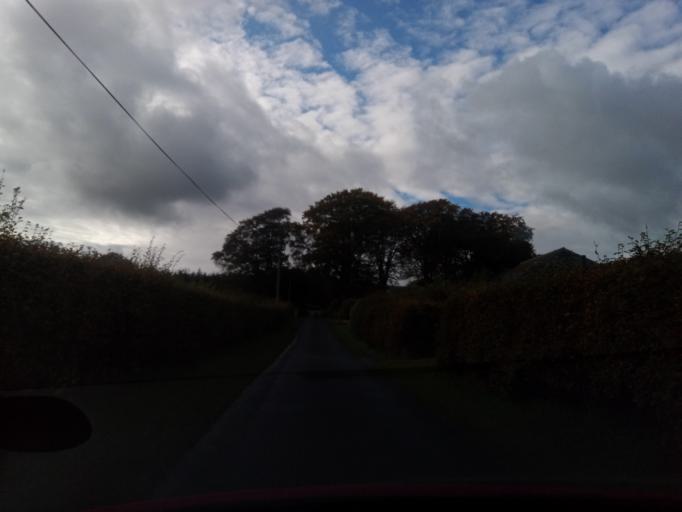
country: GB
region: Scotland
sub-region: The Scottish Borders
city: Galashiels
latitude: 55.6749
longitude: -2.8268
